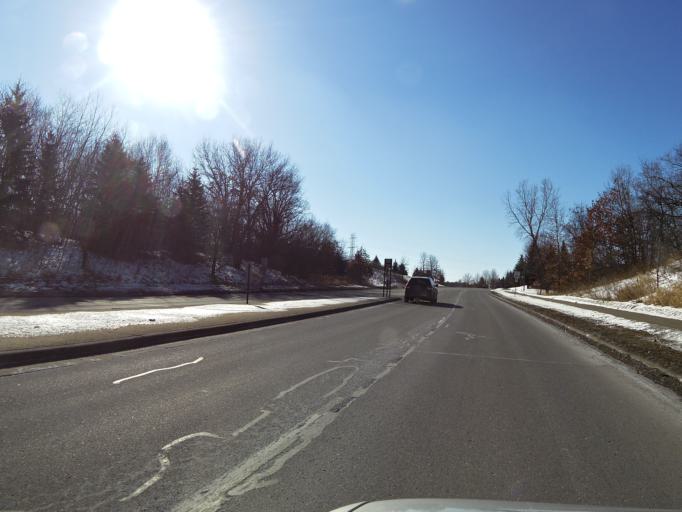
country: US
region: Minnesota
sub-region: Washington County
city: Woodbury
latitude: 44.9113
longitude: -92.9751
